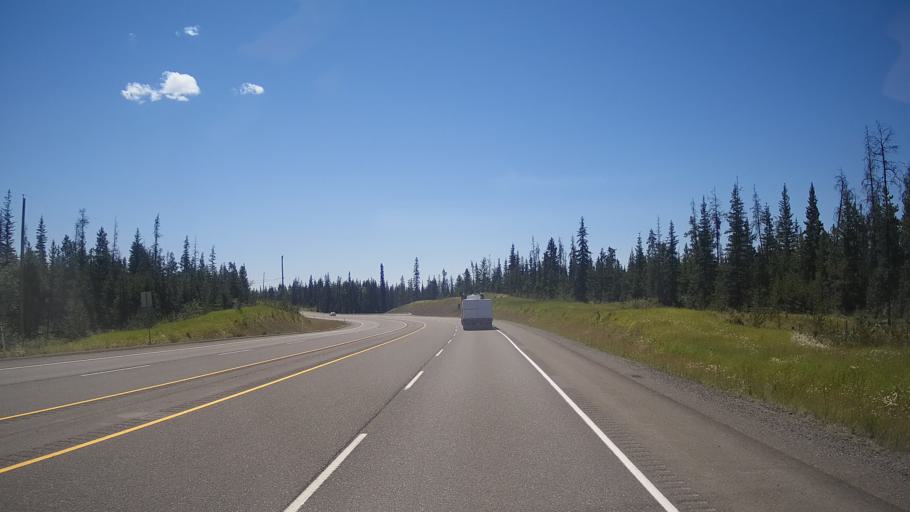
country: CA
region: British Columbia
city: Cache Creek
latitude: 51.3978
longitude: -121.3733
